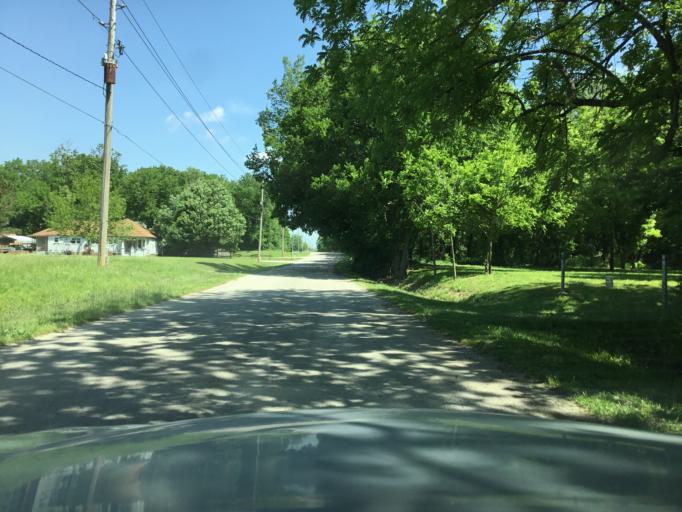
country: US
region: Kansas
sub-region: Labette County
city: Parsons
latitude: 37.3469
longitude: -95.2496
